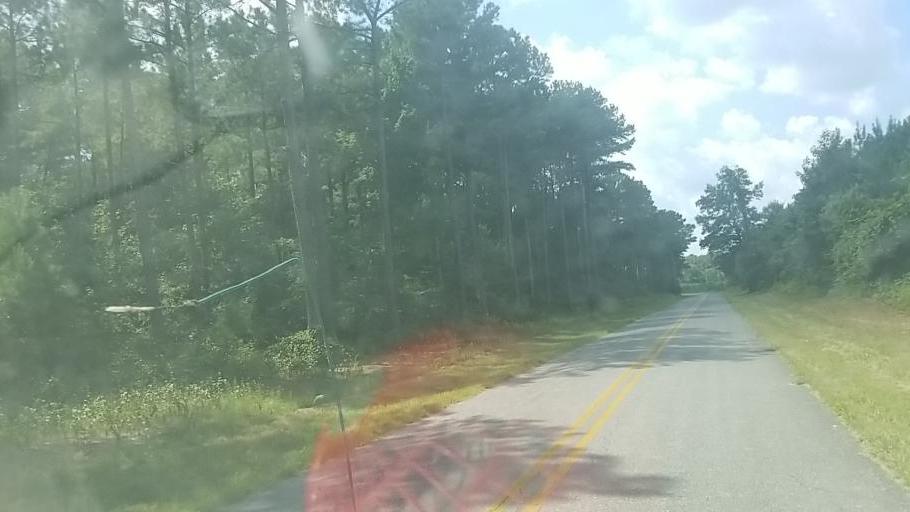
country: US
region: Maryland
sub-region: Worcester County
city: Snow Hill
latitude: 38.2570
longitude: -75.3849
